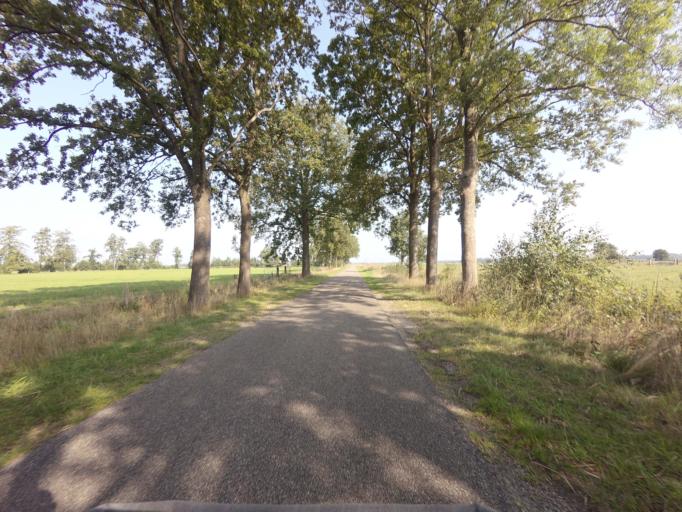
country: NL
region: Drenthe
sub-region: Gemeente Tynaarlo
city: Vries
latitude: 53.1406
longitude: 6.5311
